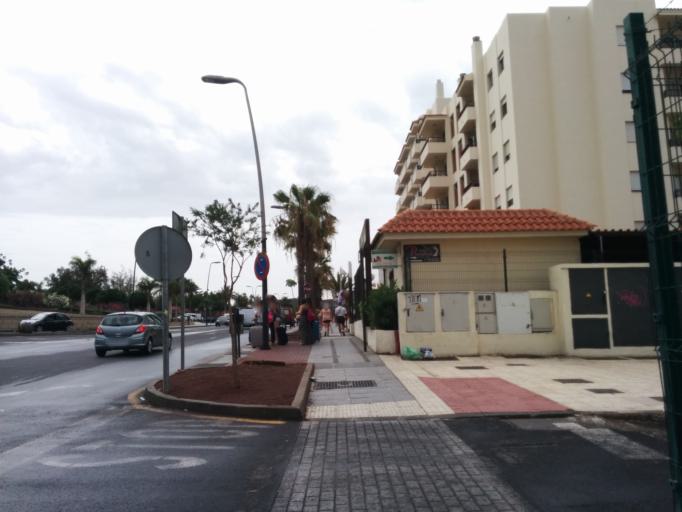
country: ES
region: Canary Islands
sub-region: Provincia de Santa Cruz de Tenerife
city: Playa de las Americas
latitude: 28.0646
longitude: -16.7276
